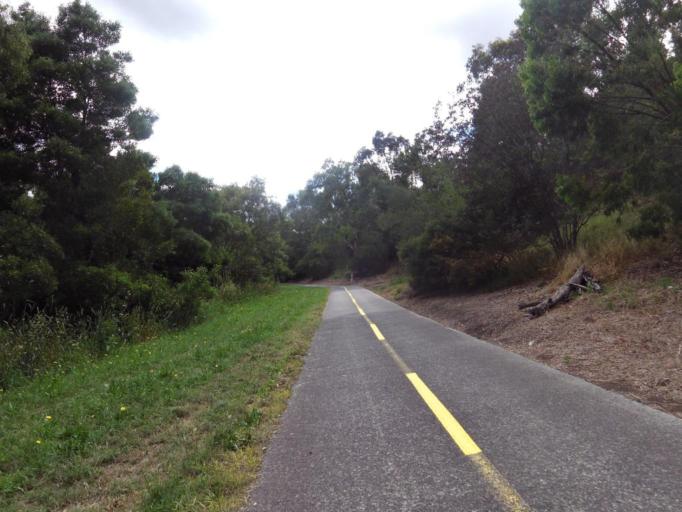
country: AU
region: Victoria
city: Heidelberg West
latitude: -37.7486
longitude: 145.0346
